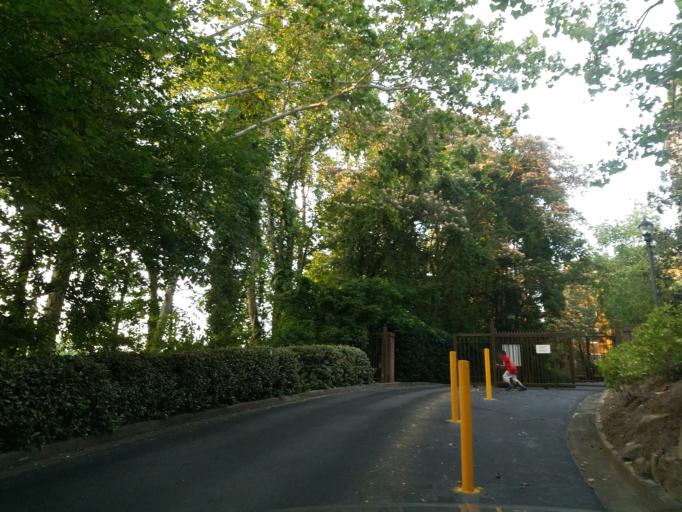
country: US
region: Georgia
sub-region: Cobb County
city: Vinings
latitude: 33.8505
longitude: -84.4329
